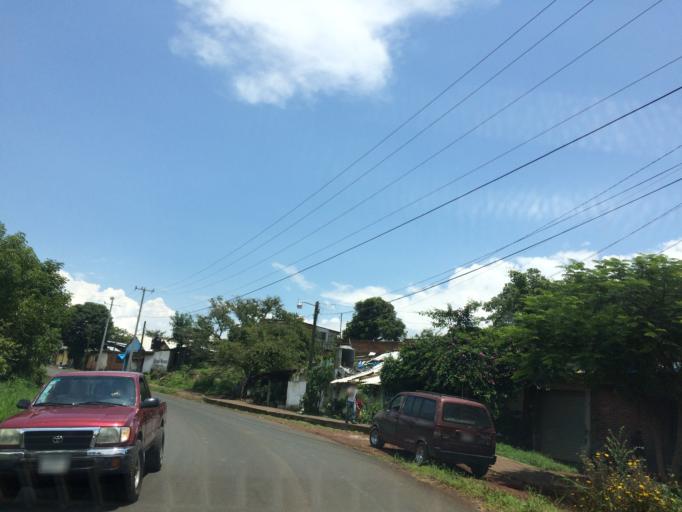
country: MX
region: Michoacan
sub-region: Periban
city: San Francisco Periban
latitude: 19.5515
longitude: -102.3985
